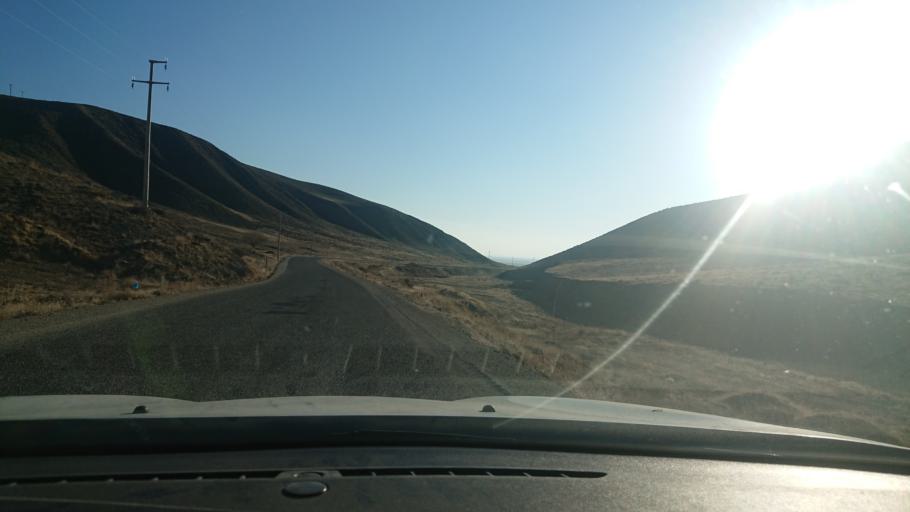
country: TR
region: Aksaray
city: Acipinar
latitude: 38.6893
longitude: 33.7438
